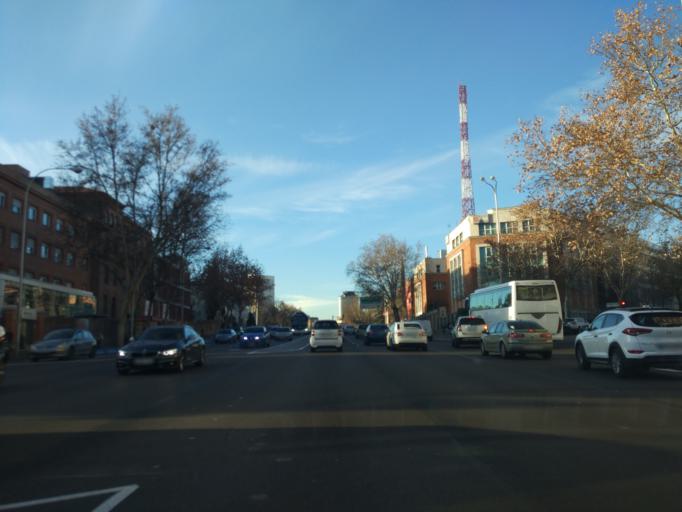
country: ES
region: Madrid
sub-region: Provincia de Madrid
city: Salamanca
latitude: 40.4424
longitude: -3.6825
